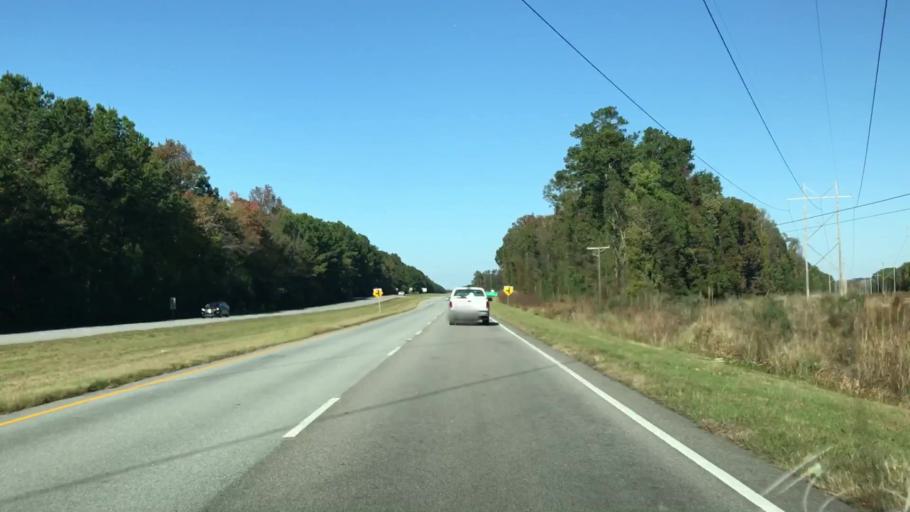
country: US
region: South Carolina
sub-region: Hampton County
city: Yemassee
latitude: 32.6100
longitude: -80.8102
